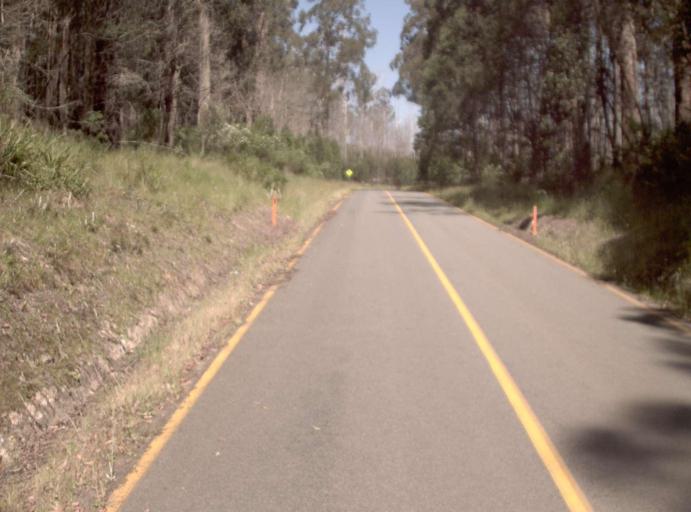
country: AU
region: Victoria
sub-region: Yarra Ranges
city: Millgrove
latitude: -37.5583
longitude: 145.8825
